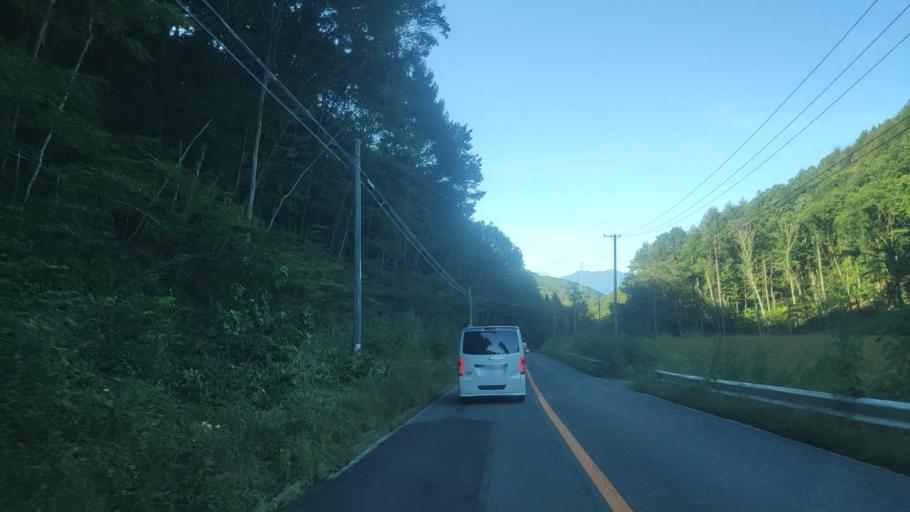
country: JP
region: Nagano
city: Kamimaruko
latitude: 36.2289
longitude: 138.2983
